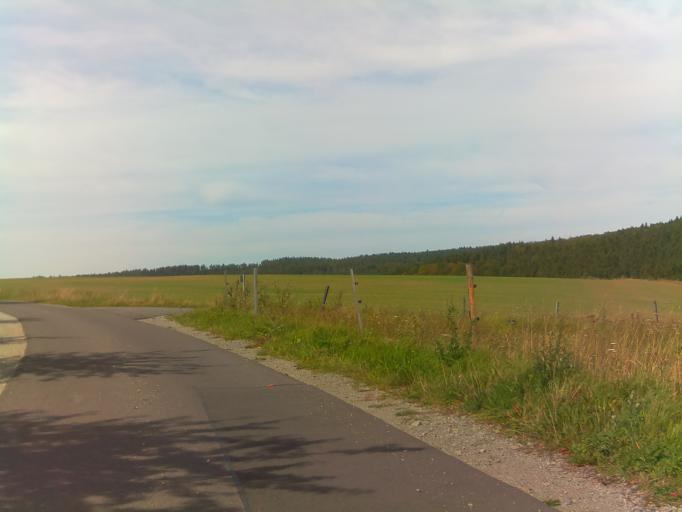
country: DE
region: Thuringia
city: Metzels
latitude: 50.6466
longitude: 10.4494
